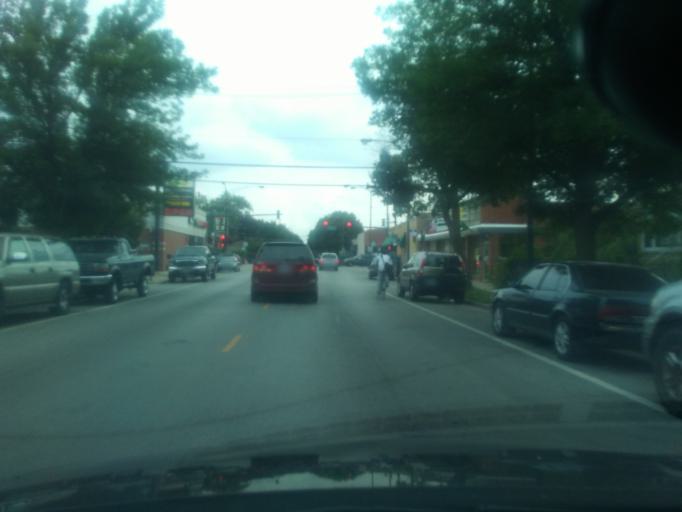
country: US
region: Illinois
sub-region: Cook County
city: Evanston
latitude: 42.0128
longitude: -87.6997
